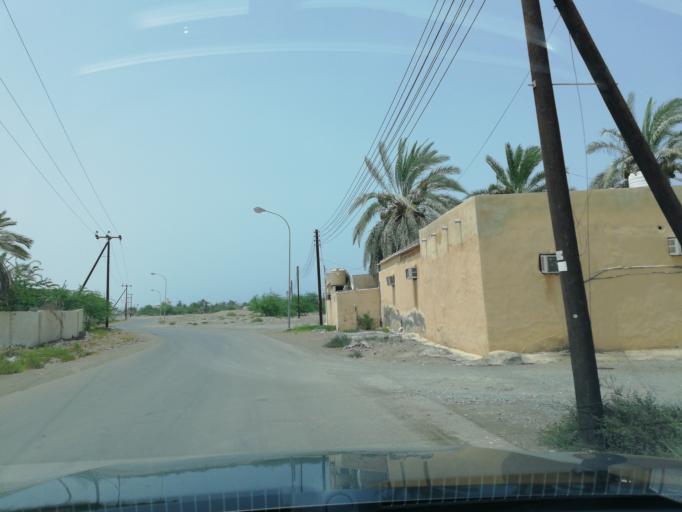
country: OM
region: Al Batinah
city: Al Liwa'
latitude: 24.6122
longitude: 56.5373
